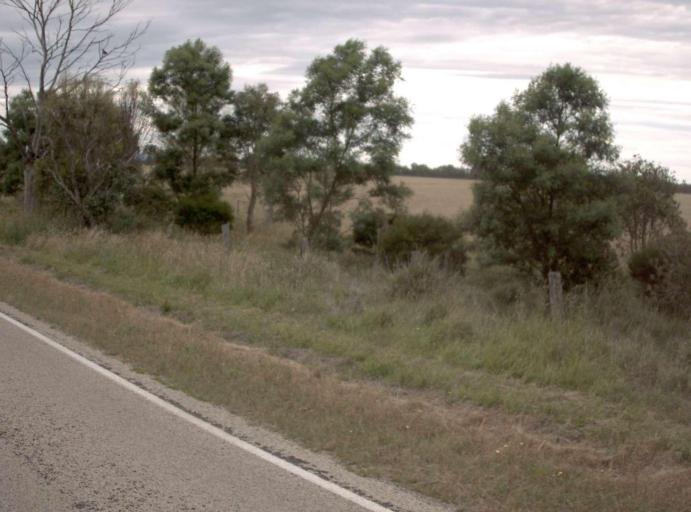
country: AU
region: Victoria
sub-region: East Gippsland
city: Bairnsdale
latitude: -37.9054
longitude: 147.5517
